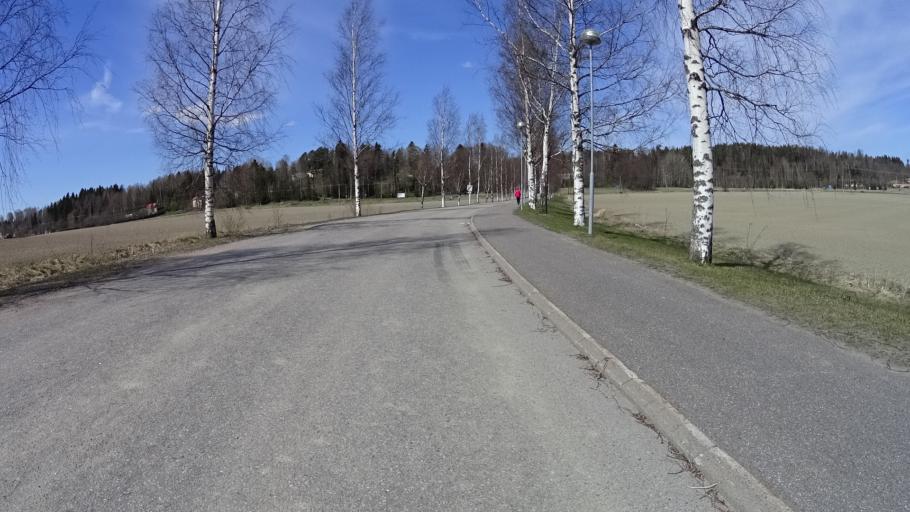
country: FI
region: Uusimaa
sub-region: Helsinki
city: Siuntio
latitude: 60.1677
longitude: 24.2047
